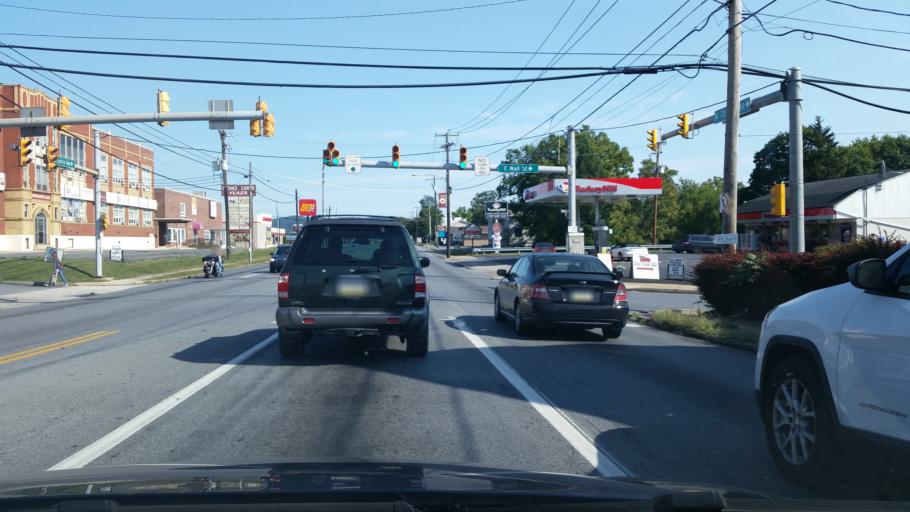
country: US
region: Pennsylvania
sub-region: Berks County
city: Leesport
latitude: 40.4489
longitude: -75.9645
